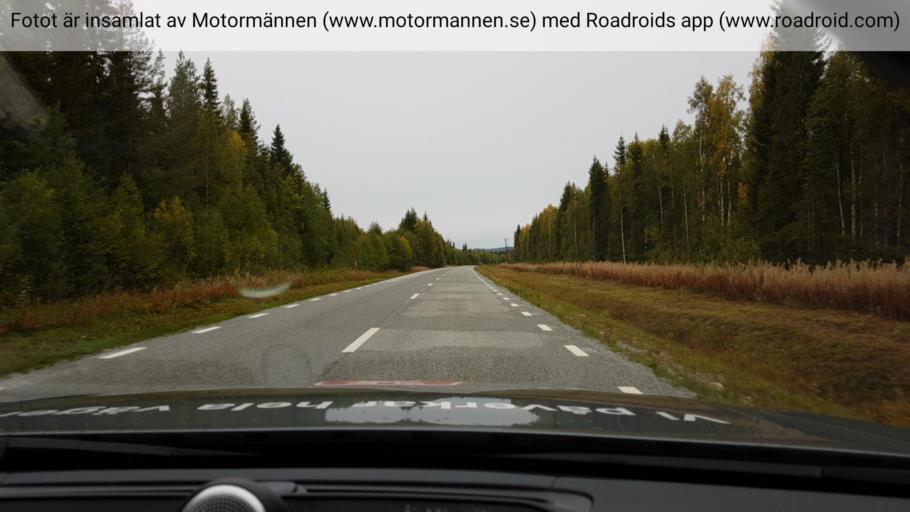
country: SE
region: Jaemtland
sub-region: Stroemsunds Kommun
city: Stroemsund
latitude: 63.9329
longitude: 15.4981
